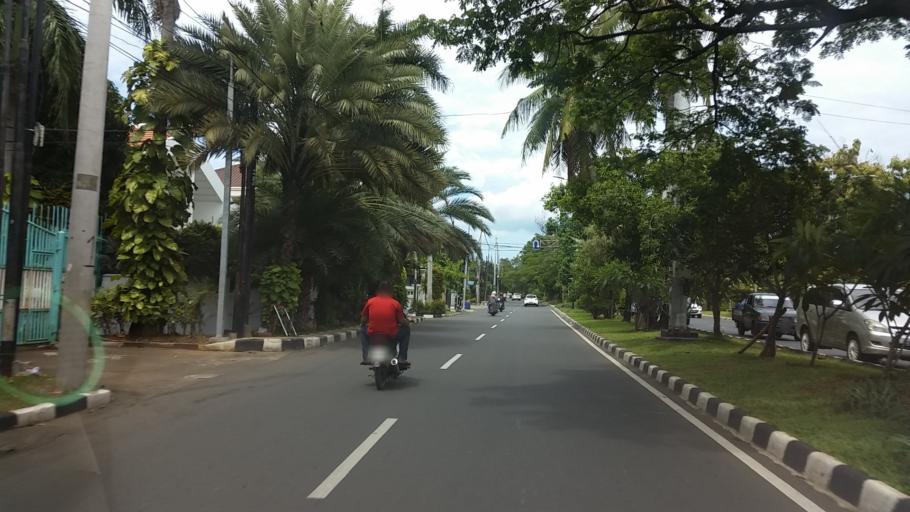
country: ID
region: Jakarta Raya
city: Jakarta
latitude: -6.1152
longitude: 106.7943
